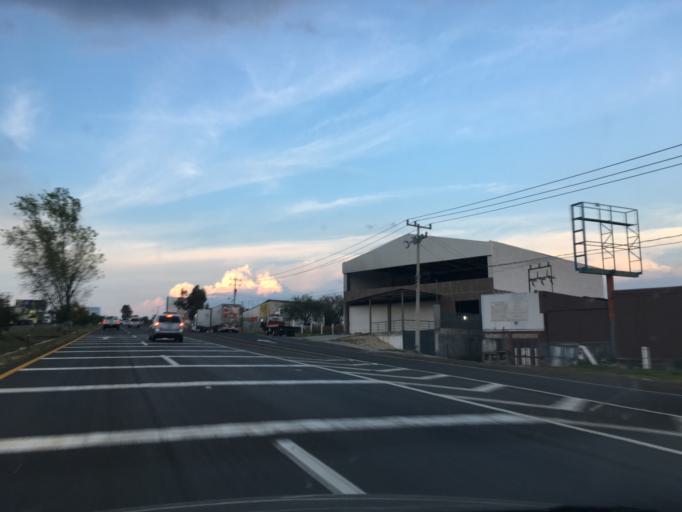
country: MX
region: Michoacan
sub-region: Morelia
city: La Mintzita (Piedra Dura)
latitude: 19.6223
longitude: -101.2800
